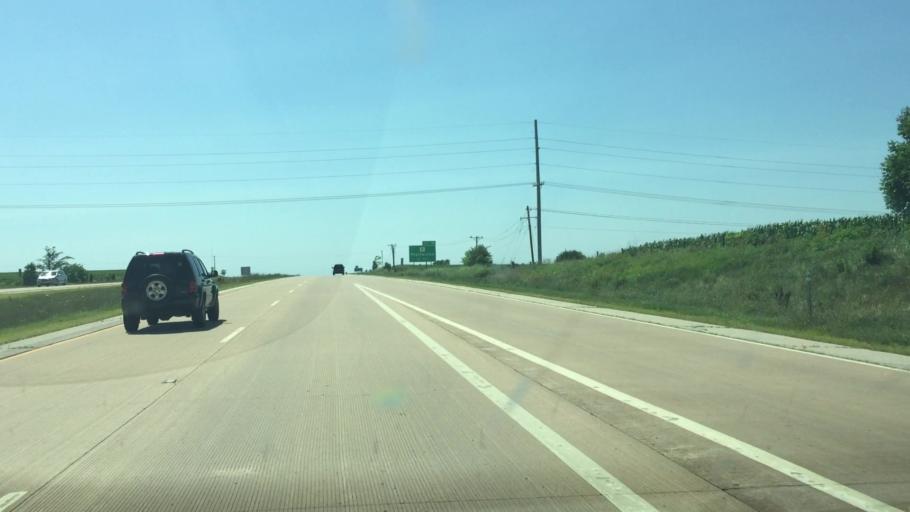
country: US
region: Wisconsin
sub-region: Grant County
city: Platteville
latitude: 42.7136
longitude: -90.4642
